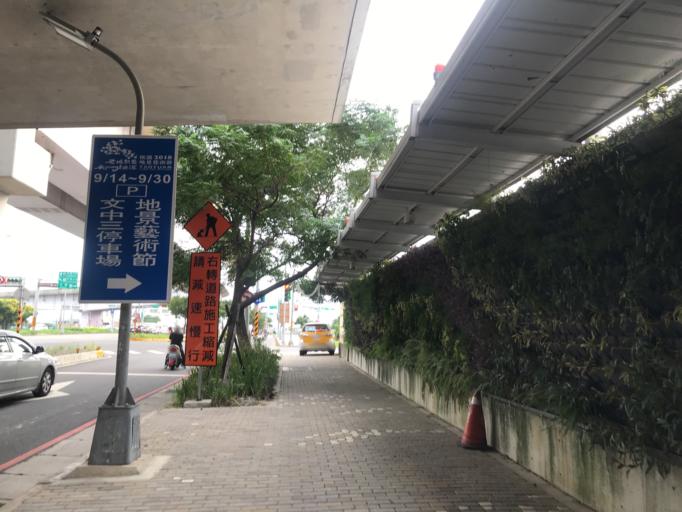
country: TW
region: Taiwan
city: Taoyuan City
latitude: 25.0017
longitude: 121.2024
